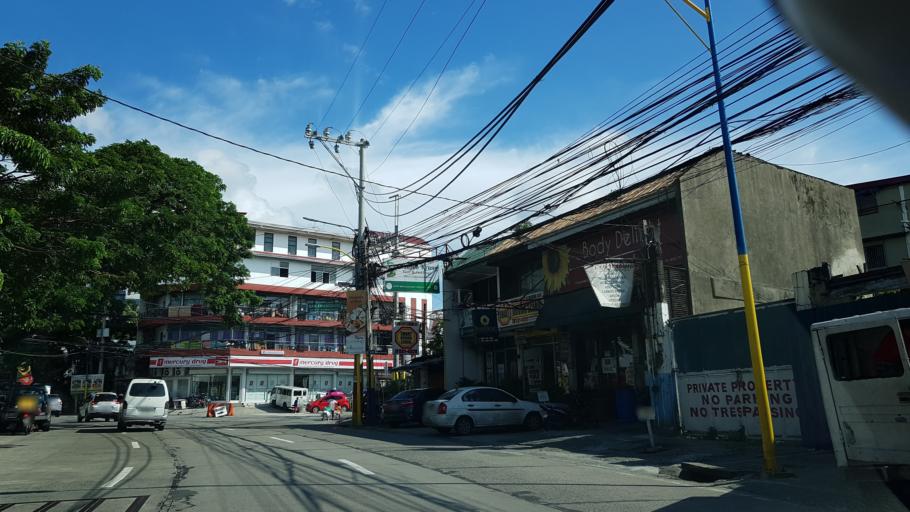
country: PH
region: Metro Manila
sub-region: Mandaluyong
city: Mandaluyong City
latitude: 14.5772
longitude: 121.0329
